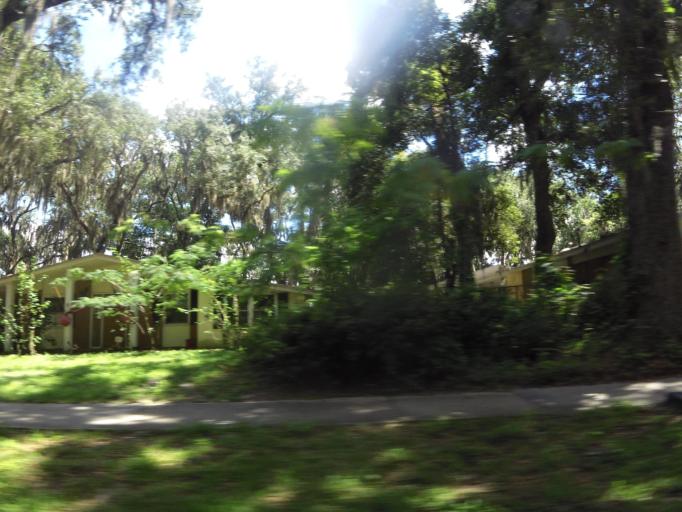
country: US
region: Florida
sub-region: Nassau County
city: Fernandina Beach
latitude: 30.6666
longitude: -81.4457
